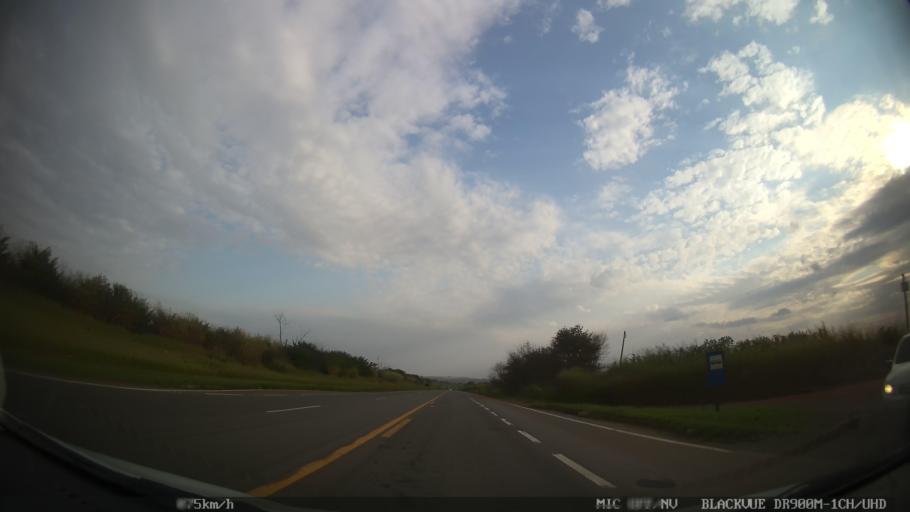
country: BR
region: Sao Paulo
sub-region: Cosmopolis
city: Cosmopolis
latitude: -22.6196
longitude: -47.2503
